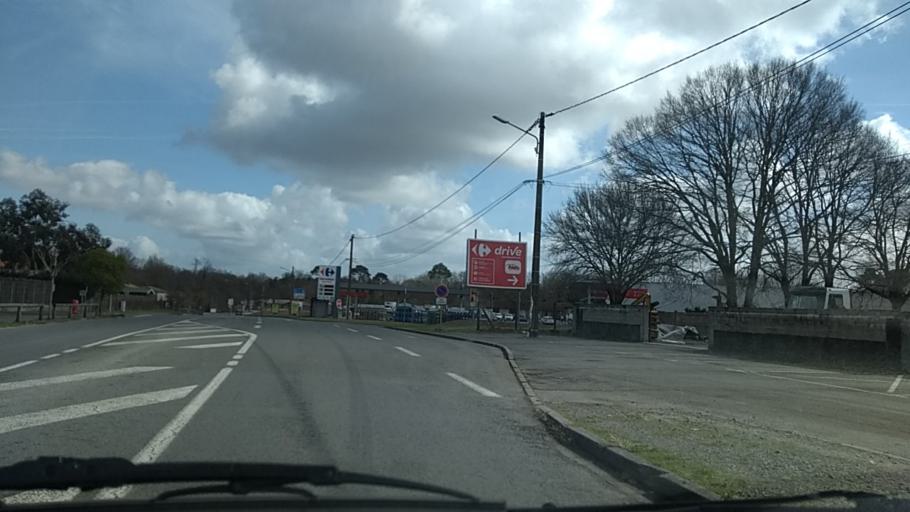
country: FR
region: Aquitaine
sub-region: Departement de la Gironde
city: Salles
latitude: 44.5477
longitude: -0.8756
